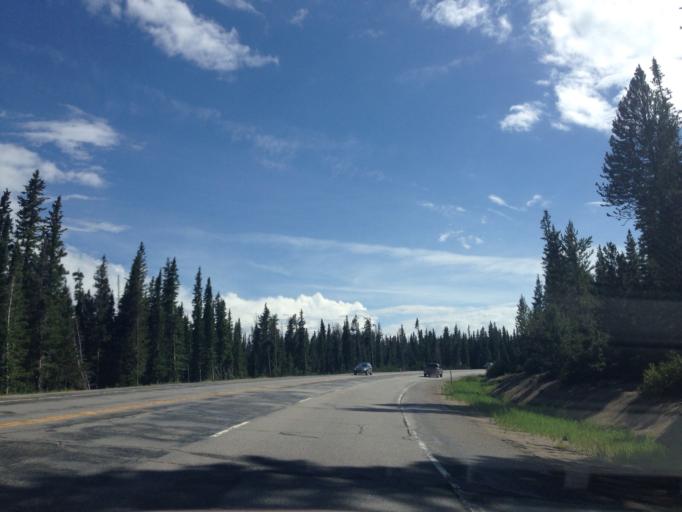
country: US
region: Colorado
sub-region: Routt County
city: Steamboat Springs
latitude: 40.3859
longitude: -106.6100
